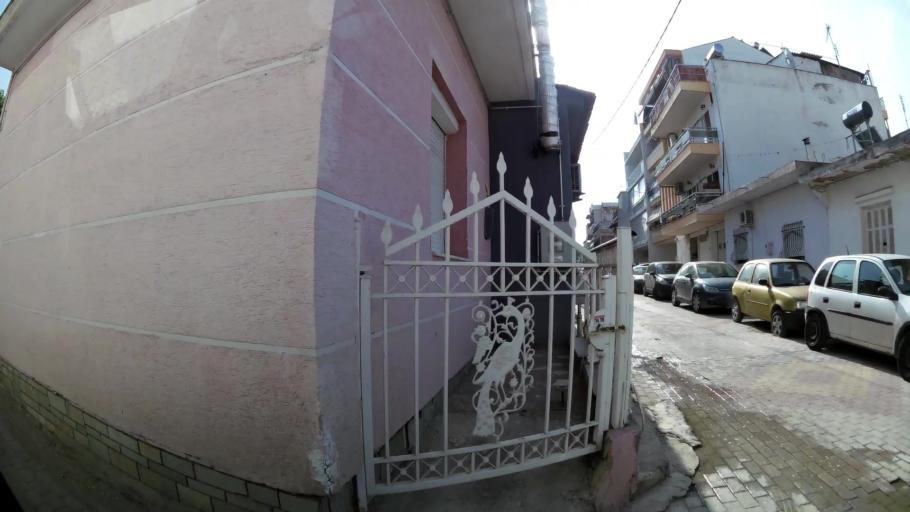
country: GR
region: Central Macedonia
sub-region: Nomos Thessalonikis
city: Evosmos
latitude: 40.6630
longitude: 22.9133
